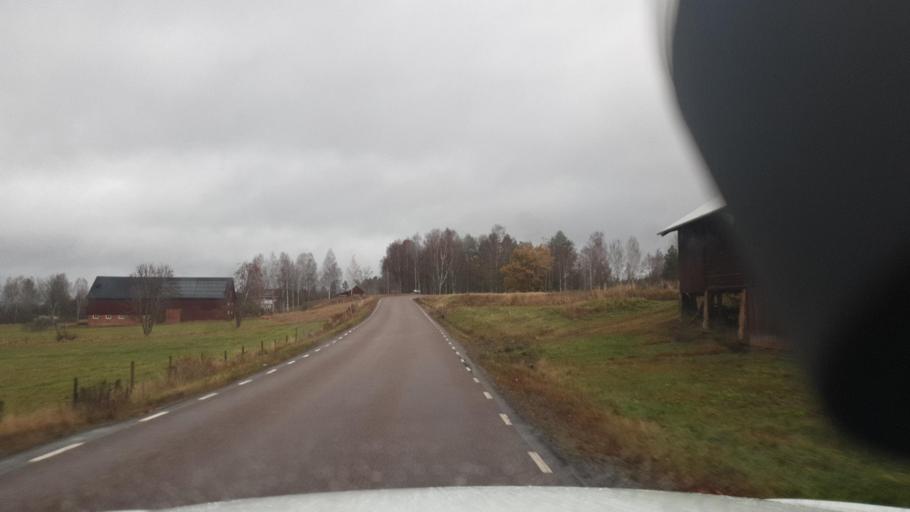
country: SE
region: Vaermland
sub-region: Eda Kommun
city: Charlottenberg
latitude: 59.7779
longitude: 12.2110
